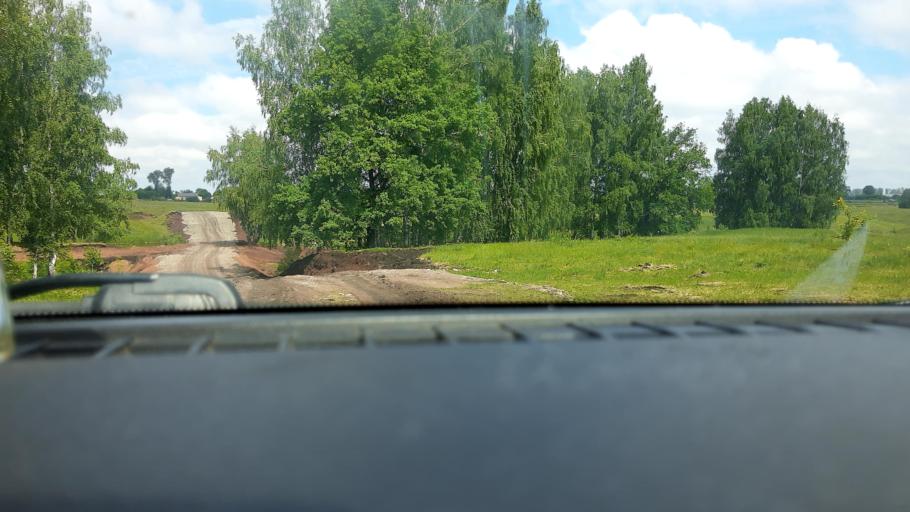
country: RU
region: Bashkortostan
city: Dmitriyevka
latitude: 54.7135
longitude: 55.4931
